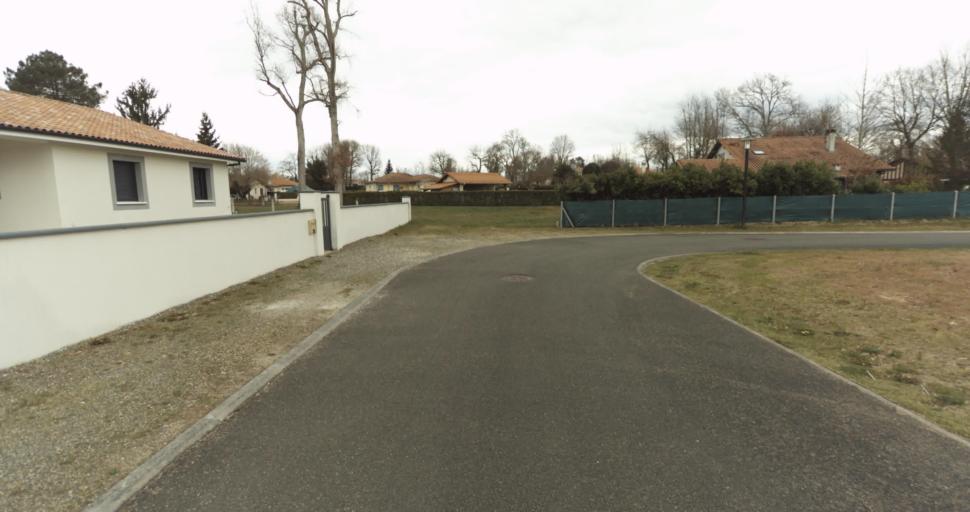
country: FR
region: Aquitaine
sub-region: Departement des Landes
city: Roquefort
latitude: 44.0335
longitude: -0.3122
